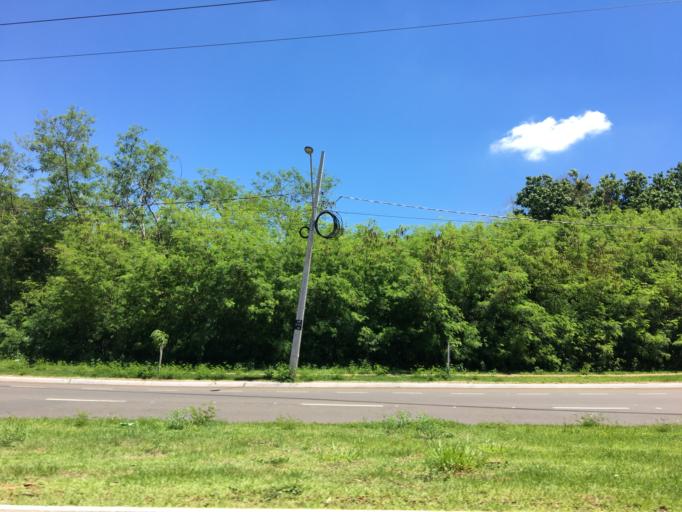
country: BR
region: Parana
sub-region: Maringa
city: Maringa
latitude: -23.4513
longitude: -51.9704
